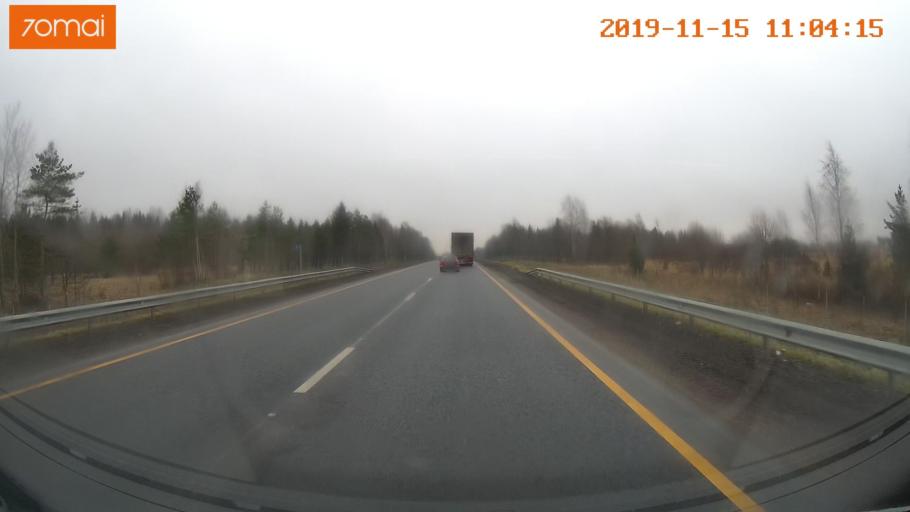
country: RU
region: Vologda
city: Chebsara
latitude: 59.1210
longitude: 38.9798
